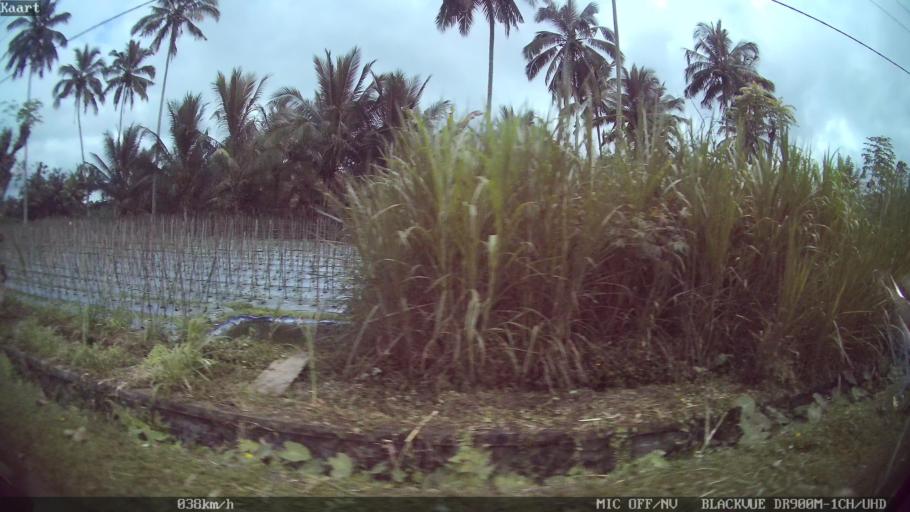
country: ID
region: Bali
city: Banjar Geriana Kangin
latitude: -8.4206
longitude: 115.4363
